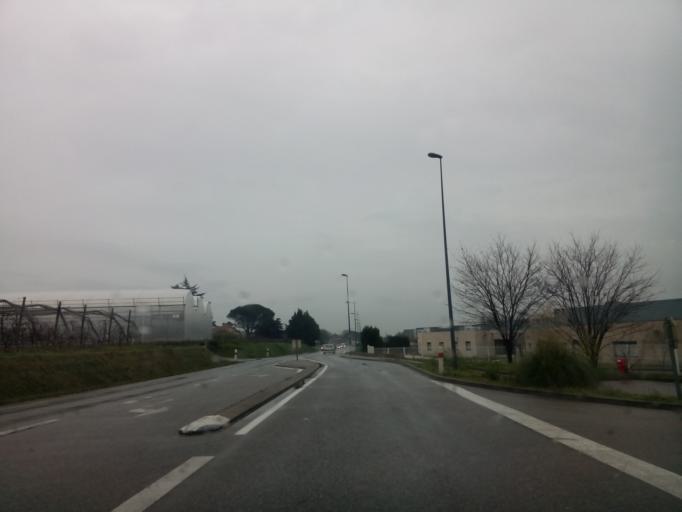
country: FR
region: Rhone-Alpes
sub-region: Departement de la Drome
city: Clerieux
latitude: 45.0519
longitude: 4.9788
